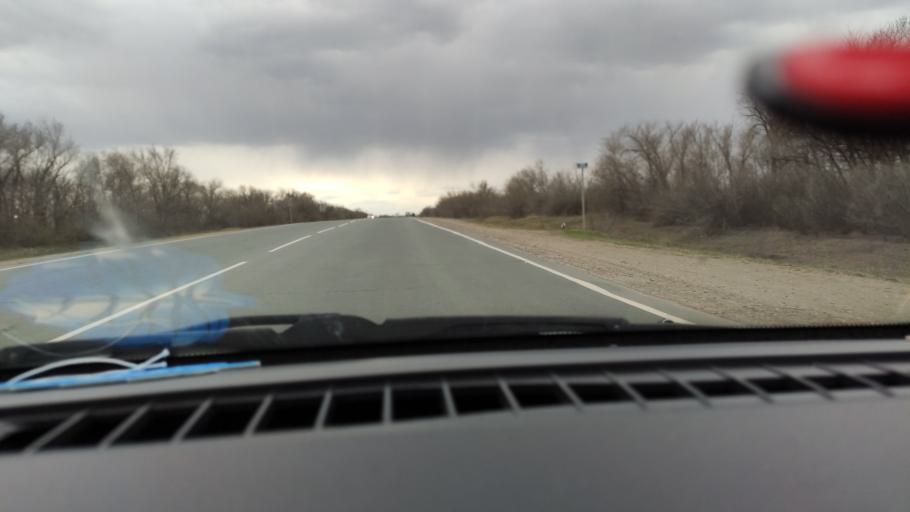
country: RU
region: Saratov
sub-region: Saratovskiy Rayon
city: Saratov
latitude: 51.7111
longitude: 46.0194
